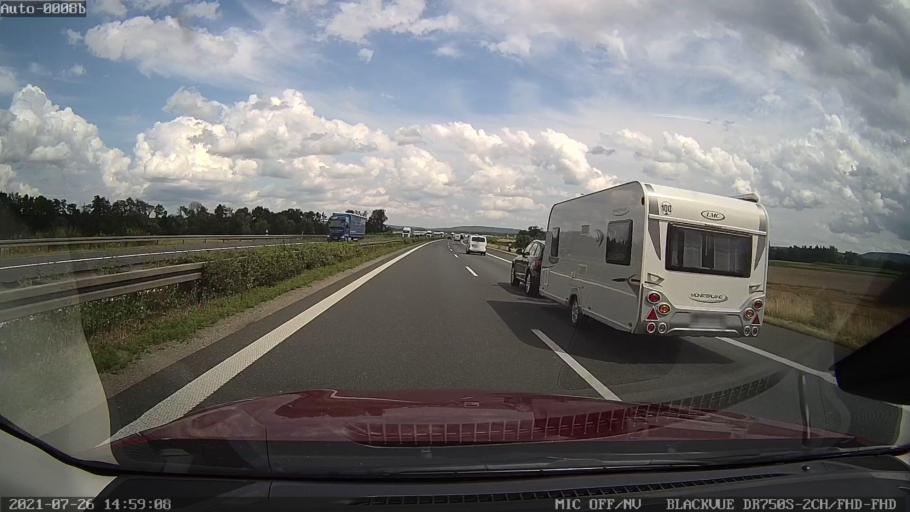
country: DE
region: Bavaria
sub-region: Regierungsbezirk Unterfranken
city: Kleinlangheim
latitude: 49.7821
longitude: 10.2755
